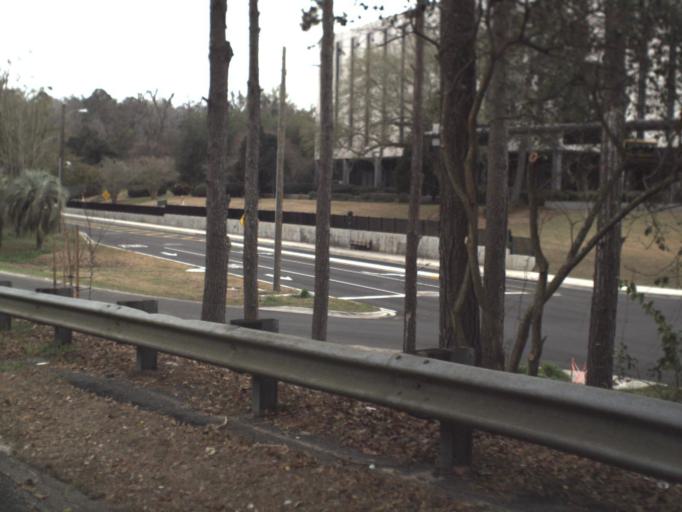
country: US
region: Florida
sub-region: Leon County
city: Tallahassee
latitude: 30.4381
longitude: -84.2753
